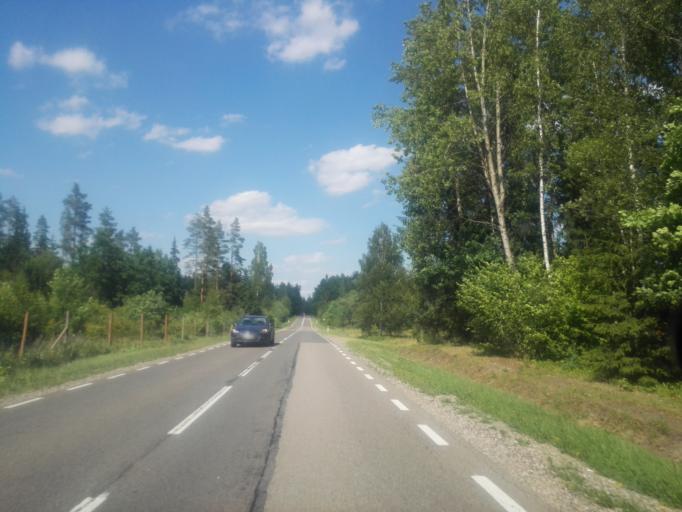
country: PL
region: Podlasie
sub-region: Powiat sejnenski
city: Sejny
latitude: 54.0040
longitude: 23.3192
